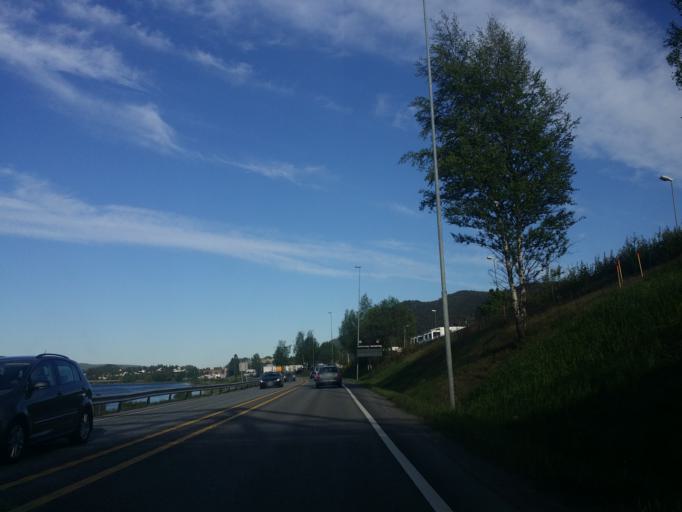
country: NO
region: Buskerud
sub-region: Nedre Eiker
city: Mjondalen
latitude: 59.7525
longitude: 10.0073
